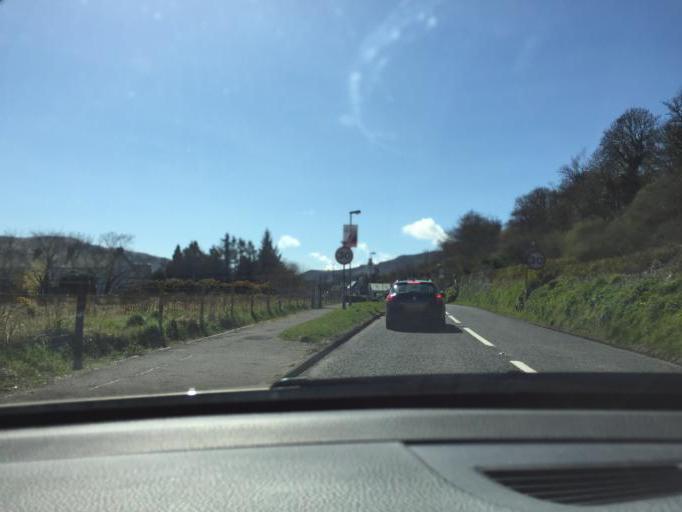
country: GB
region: Northern Ireland
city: Glenariff
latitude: 55.0624
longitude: -6.0603
